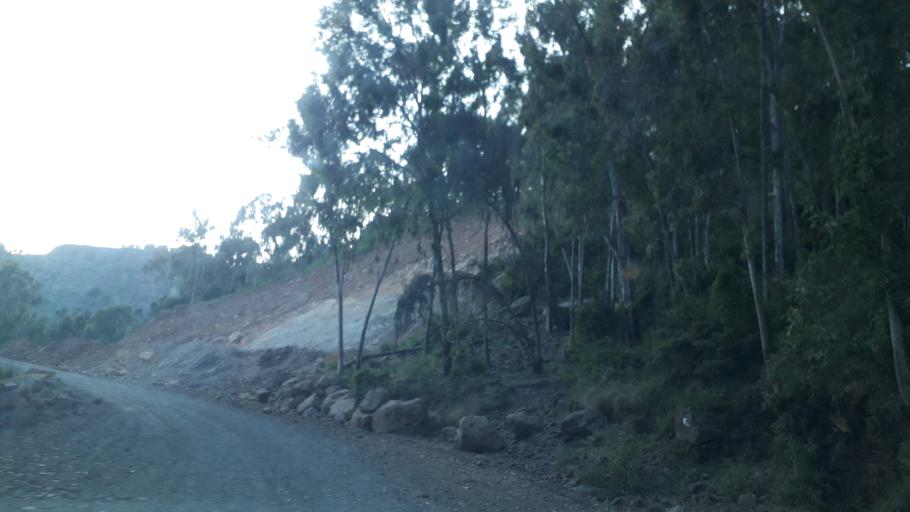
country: ET
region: Amhara
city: Lalibela
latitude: 11.5522
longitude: 39.2171
